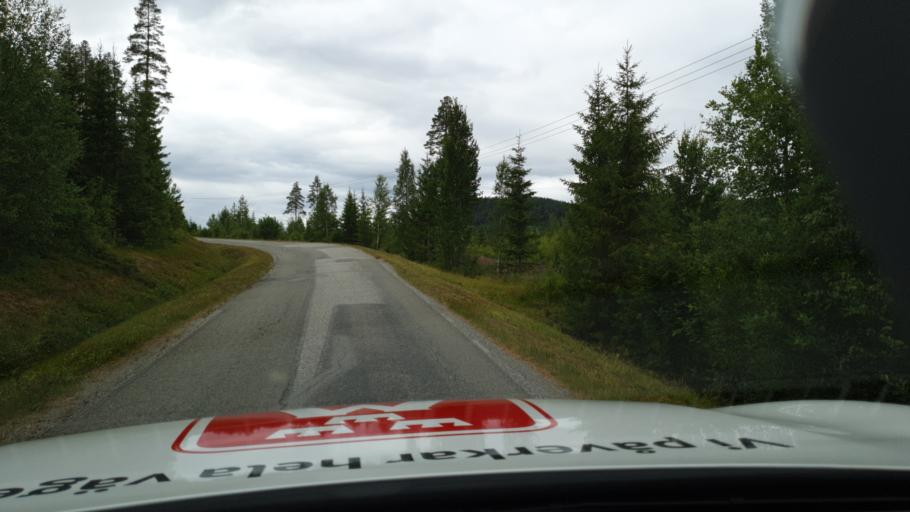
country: SE
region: Vaesterbotten
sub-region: Dorotea Kommun
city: Dorotea
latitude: 64.1264
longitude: 16.3046
